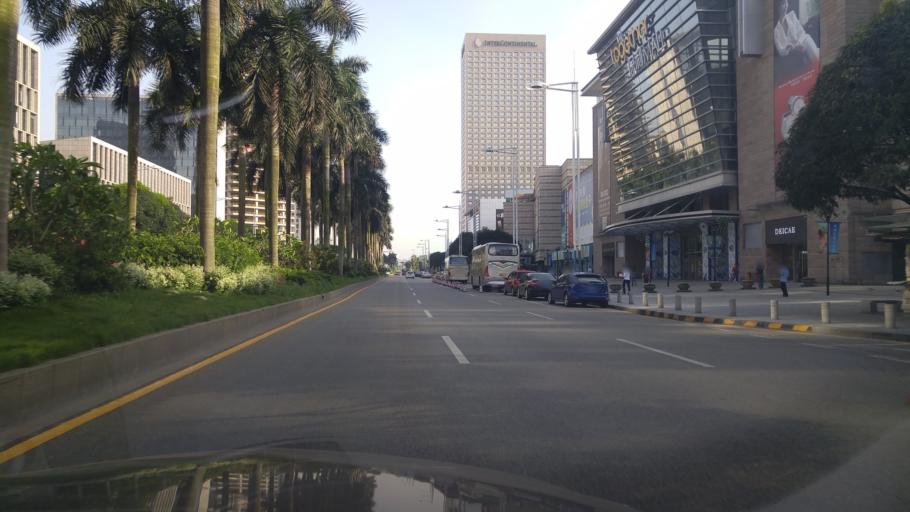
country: CN
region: Guangdong
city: Foshan
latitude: 23.0637
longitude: 113.1435
